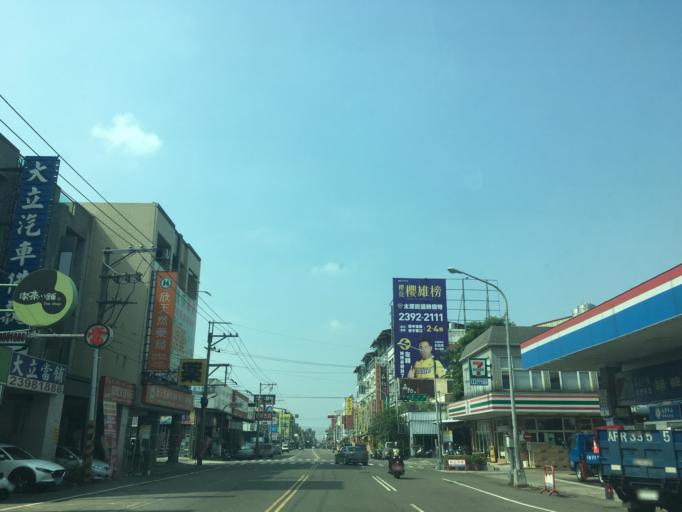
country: TW
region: Taiwan
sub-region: Taichung City
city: Taichung
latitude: 24.1580
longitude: 120.7127
